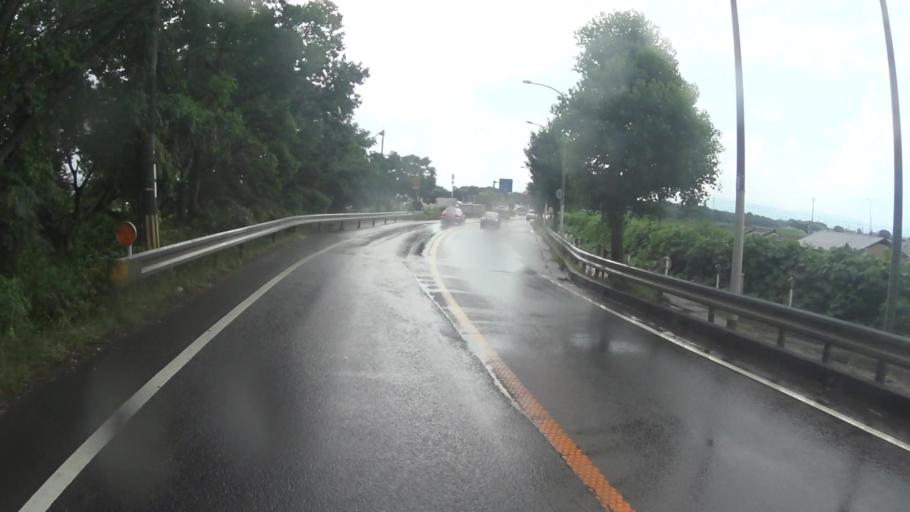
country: JP
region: Kyoto
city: Tanabe
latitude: 34.8221
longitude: 135.7974
